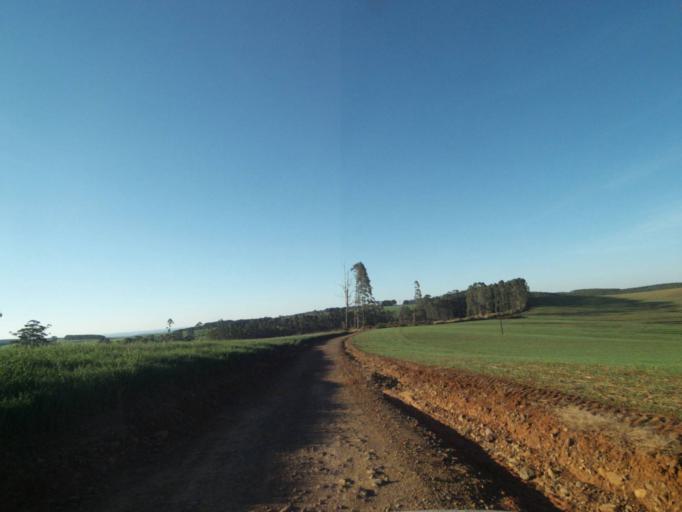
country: BR
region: Parana
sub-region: Telemaco Borba
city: Telemaco Borba
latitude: -24.4823
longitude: -50.5939
